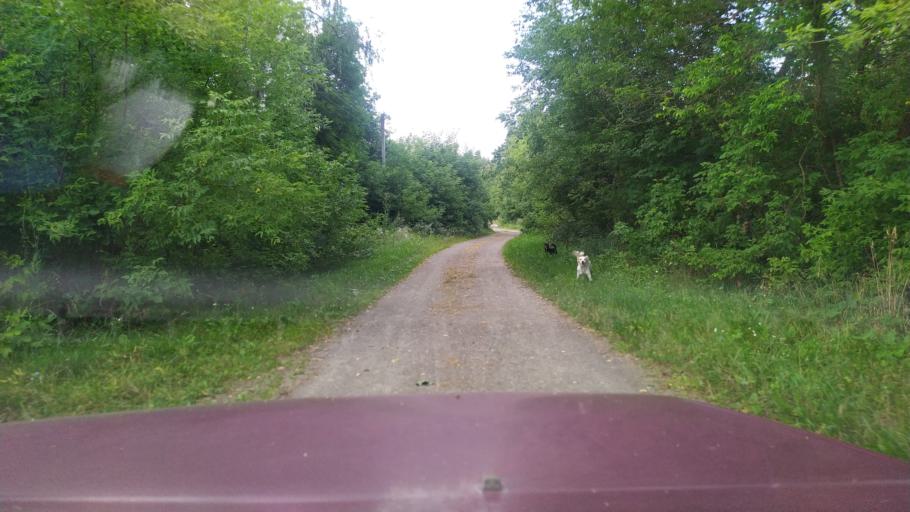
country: RU
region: Brjansk
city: Lyubovsho
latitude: 52.7480
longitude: 31.4606
